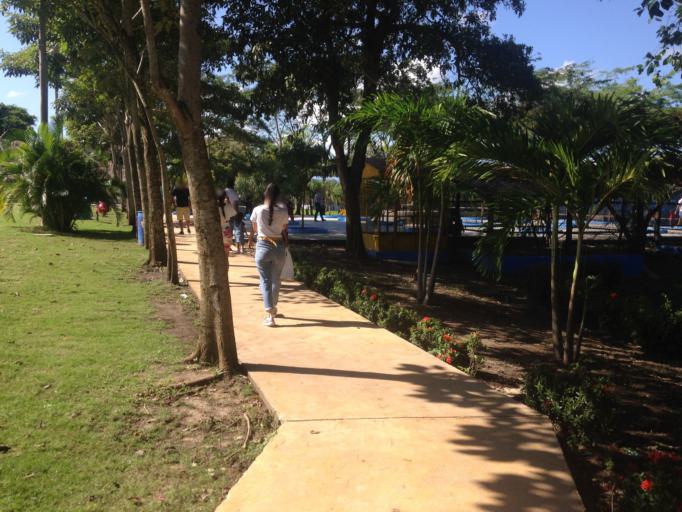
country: CO
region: Atlantico
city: Baranoa
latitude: 10.8410
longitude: -74.9024
